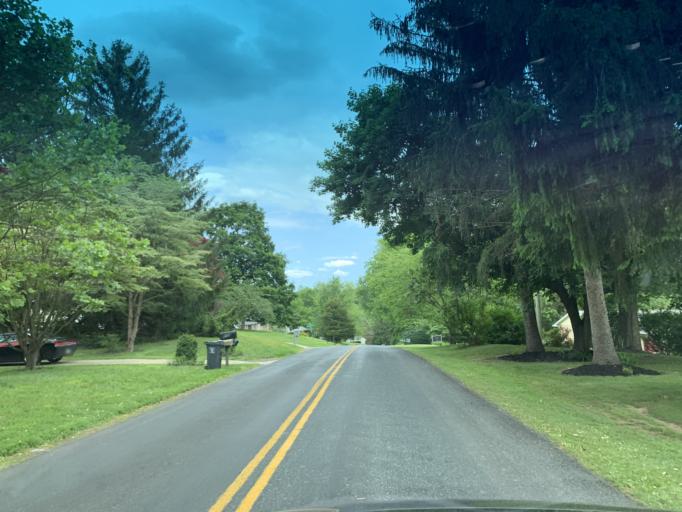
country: US
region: Maryland
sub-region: Harford County
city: Jarrettsville
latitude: 39.6298
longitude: -76.5065
